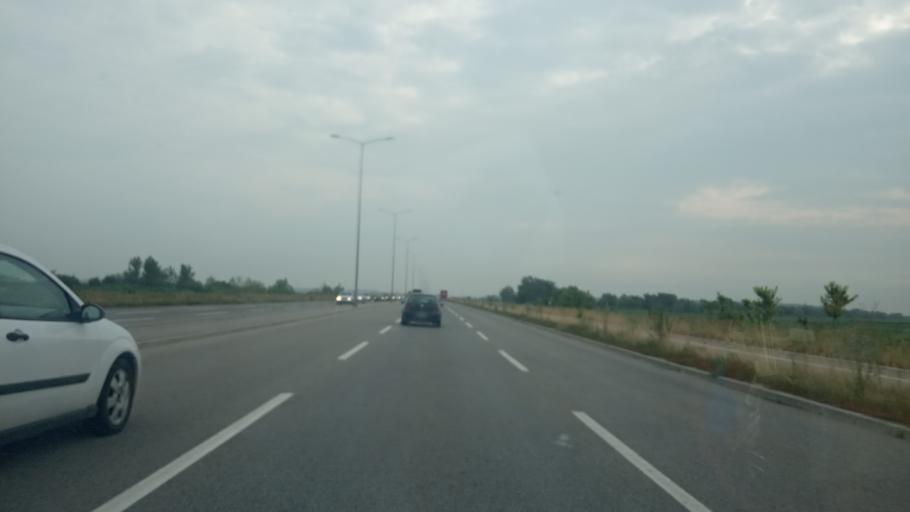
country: RS
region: Central Serbia
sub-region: Belgrade
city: Zemun
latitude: 44.8768
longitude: 20.3921
